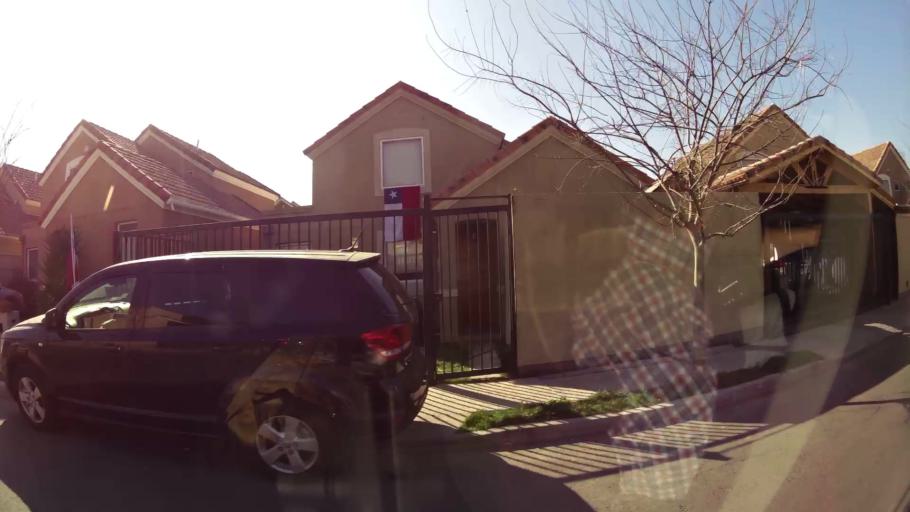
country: CL
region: Santiago Metropolitan
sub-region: Provincia de Chacabuco
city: Chicureo Abajo
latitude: -33.3460
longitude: -70.6767
